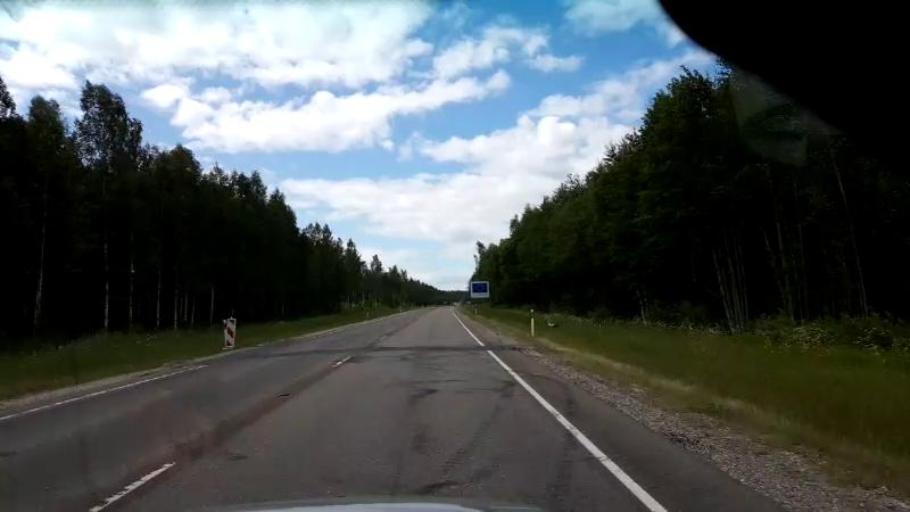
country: LV
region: Salacgrivas
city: Ainazi
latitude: 58.0115
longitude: 24.4915
